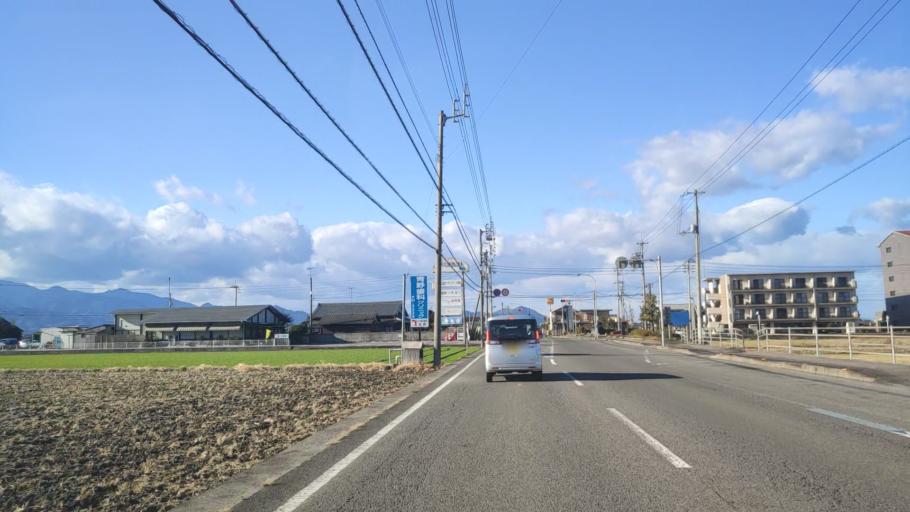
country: JP
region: Ehime
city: Saijo
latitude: 33.9133
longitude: 133.1080
